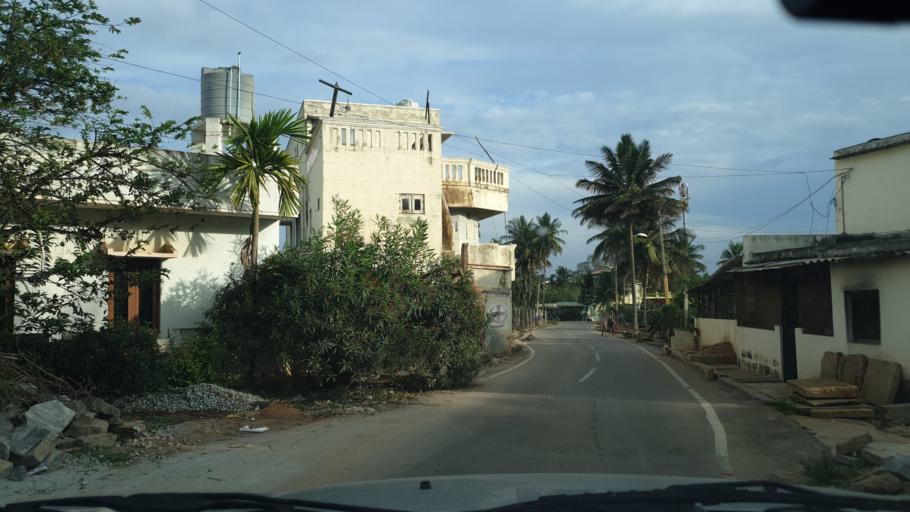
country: IN
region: Karnataka
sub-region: Bangalore Urban
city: Yelahanka
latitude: 13.1902
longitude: 77.6283
